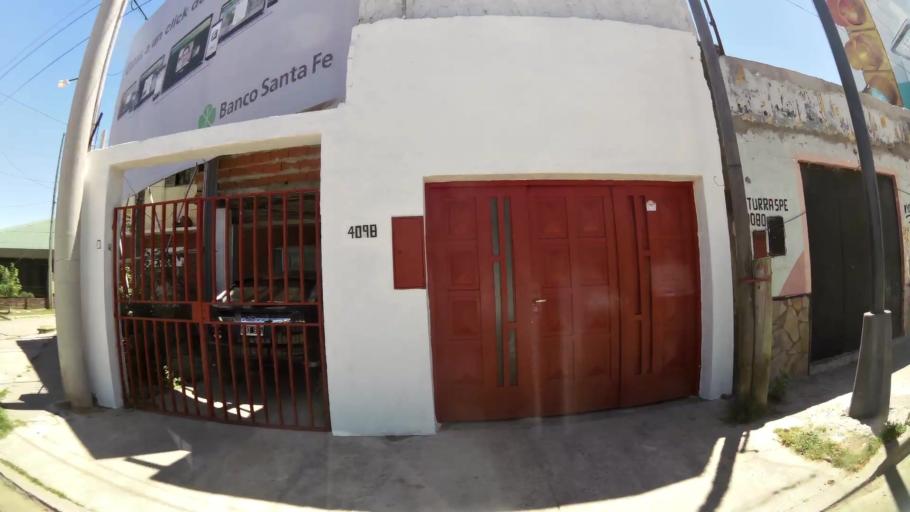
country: AR
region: Santa Fe
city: Santa Fe de la Vera Cruz
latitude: -31.6253
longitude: -60.7197
